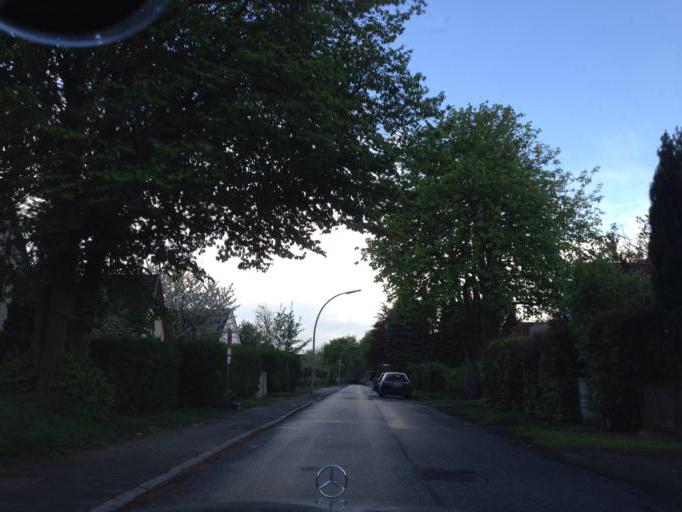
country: DE
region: Schleswig-Holstein
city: Barsbuettel
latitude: 53.5860
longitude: 10.1562
